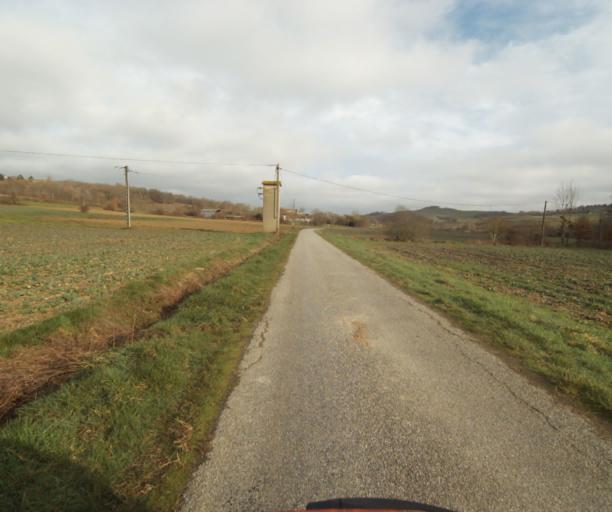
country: FR
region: Midi-Pyrenees
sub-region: Departement de l'Ariege
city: Saverdun
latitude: 43.1840
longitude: 1.5173
